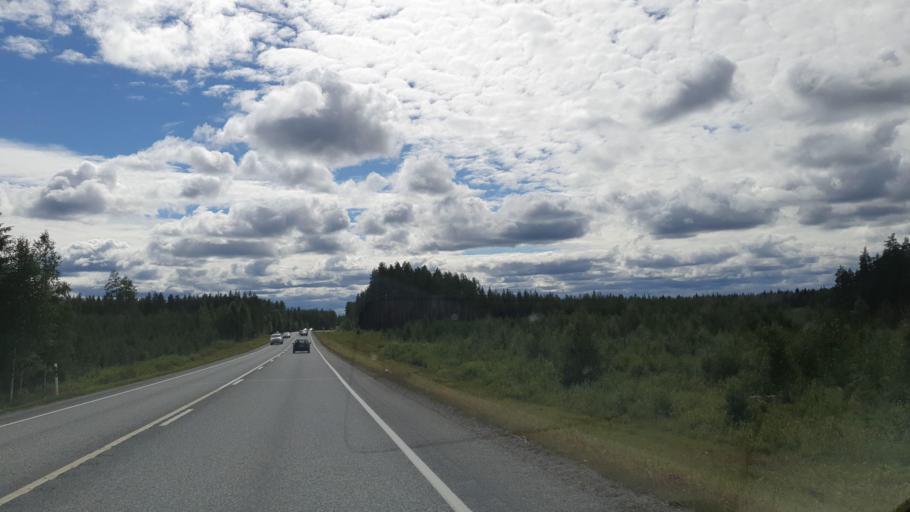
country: FI
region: Kainuu
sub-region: Kajaani
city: Kajaani
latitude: 64.1541
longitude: 27.5149
